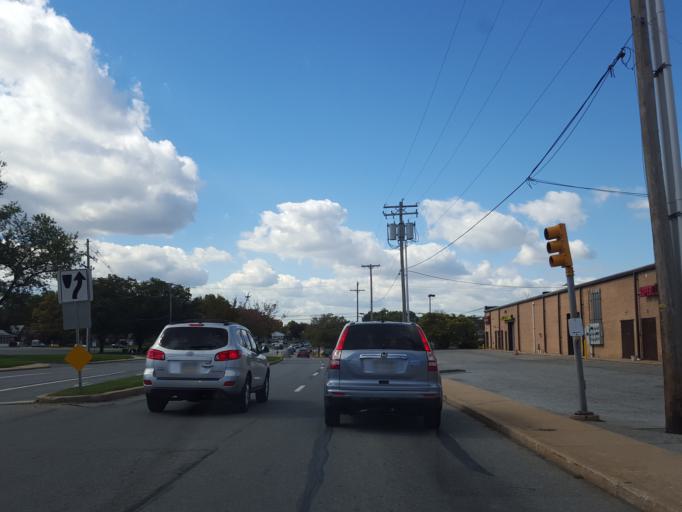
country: US
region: Pennsylvania
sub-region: York County
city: East York
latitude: 39.9731
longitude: -76.6771
